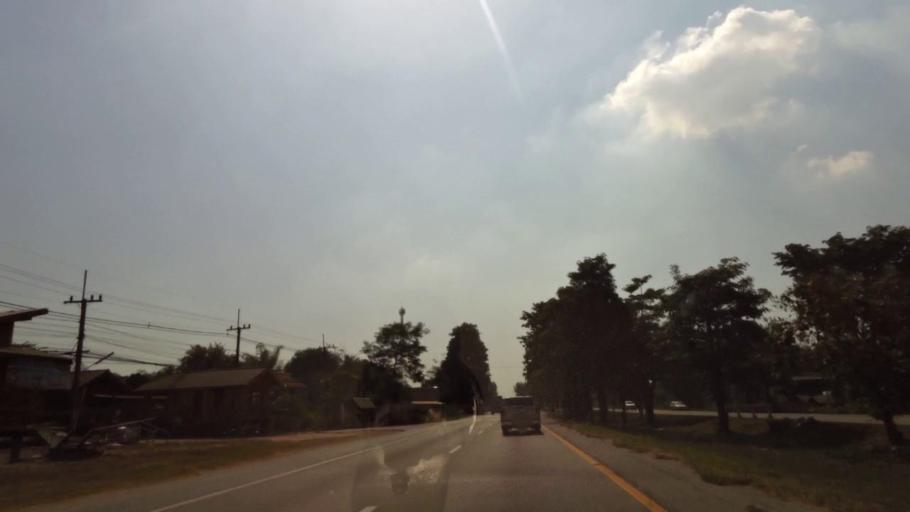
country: TH
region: Phichit
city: Wachira Barami
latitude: 16.5337
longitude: 100.1438
